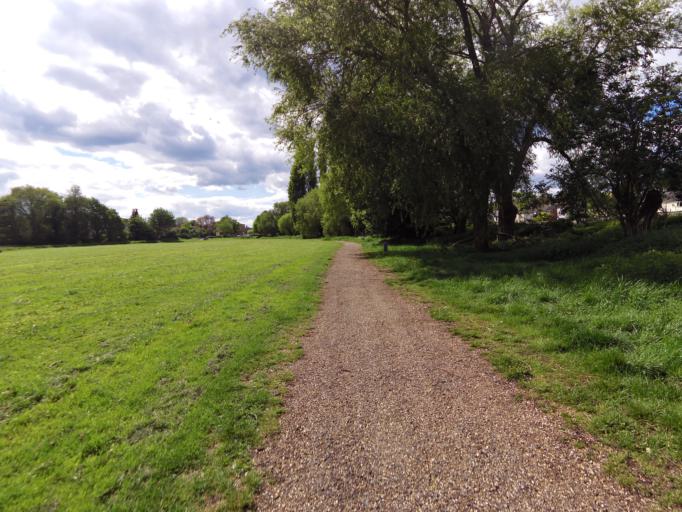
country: GB
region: England
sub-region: Suffolk
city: Bury St Edmunds
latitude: 52.2391
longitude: 0.7079
